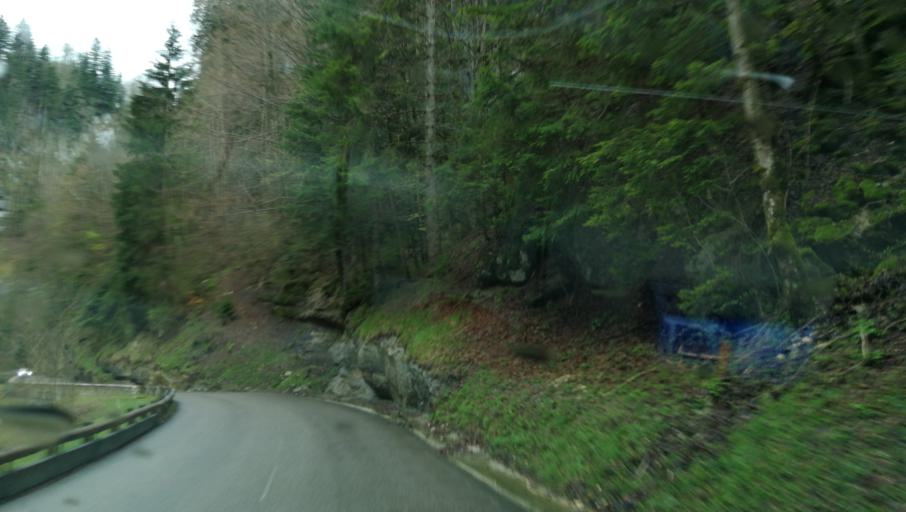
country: FR
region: Rhone-Alpes
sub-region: Departement de l'Isere
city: Villard-de-Lans
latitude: 45.0780
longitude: 5.5211
